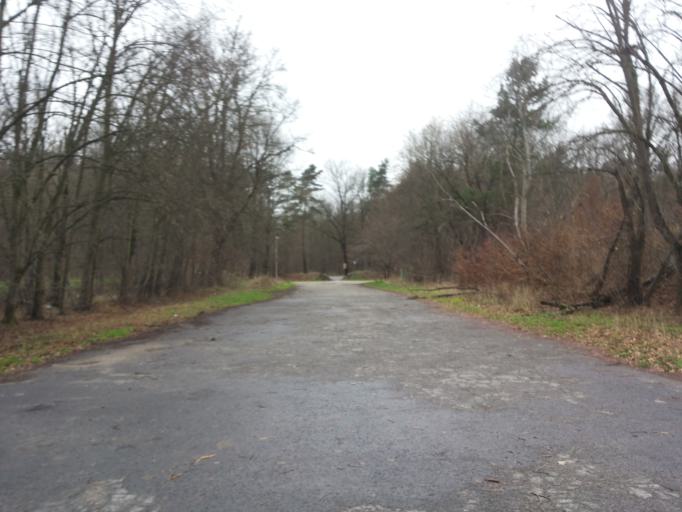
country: DE
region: Bavaria
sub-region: Regierungsbezirk Mittelfranken
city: Wendelstein
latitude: 49.4046
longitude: 11.1609
